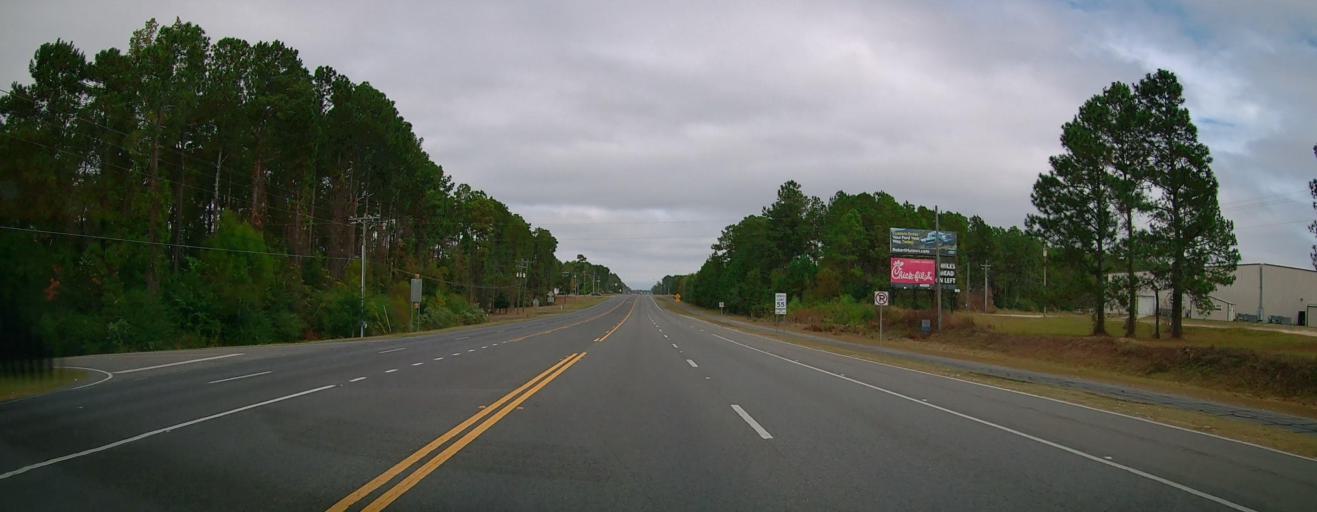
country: US
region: Georgia
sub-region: Colquitt County
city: Moultrie
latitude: 31.1039
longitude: -83.7944
